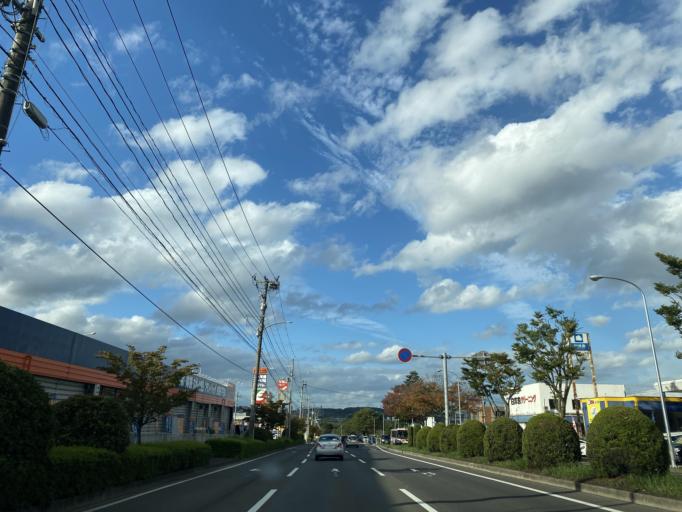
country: JP
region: Miyagi
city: Sendai-shi
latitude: 38.3183
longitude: 140.8445
